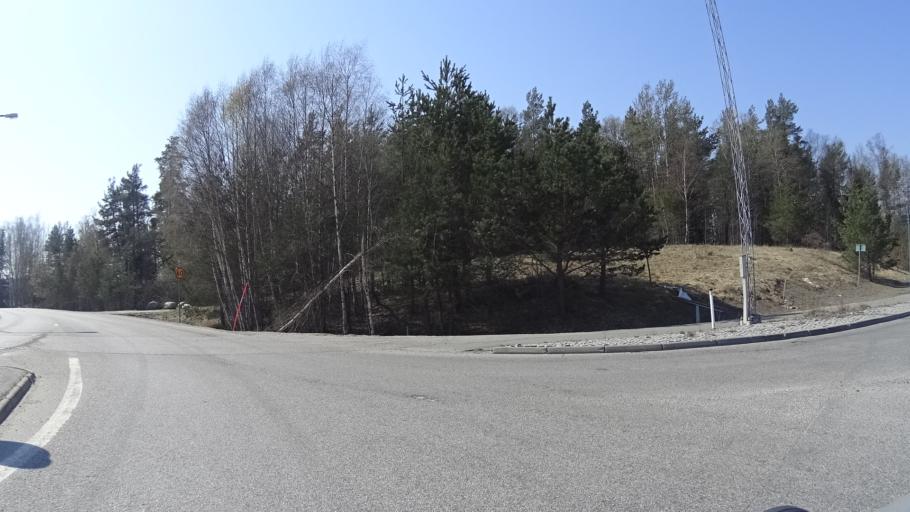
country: SE
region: Stockholm
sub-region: Haninge Kommun
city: Jordbro
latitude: 59.1084
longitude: 18.1185
